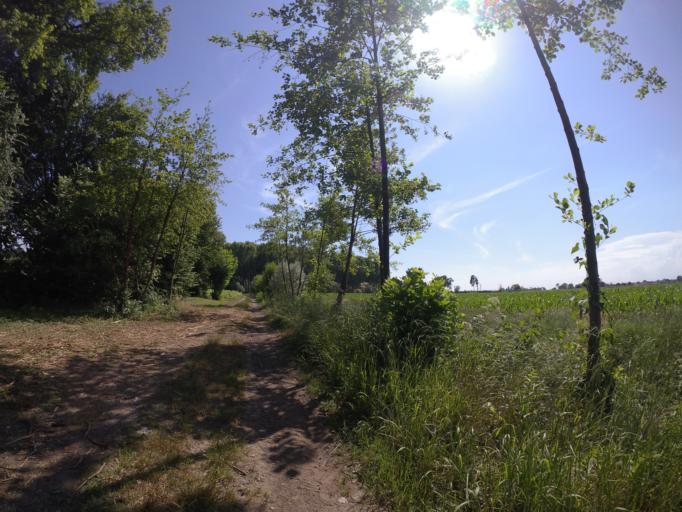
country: IT
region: Friuli Venezia Giulia
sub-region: Provincia di Udine
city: Bertiolo
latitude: 45.9351
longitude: 13.0799
